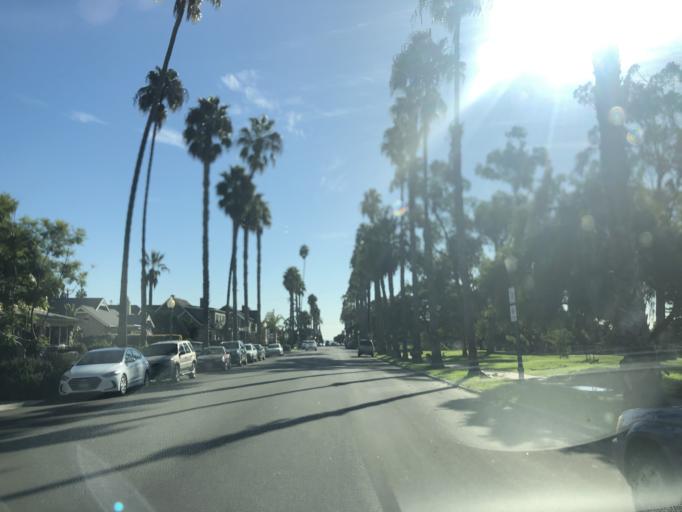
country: US
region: California
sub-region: San Diego County
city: San Diego
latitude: 32.7222
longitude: -117.1339
